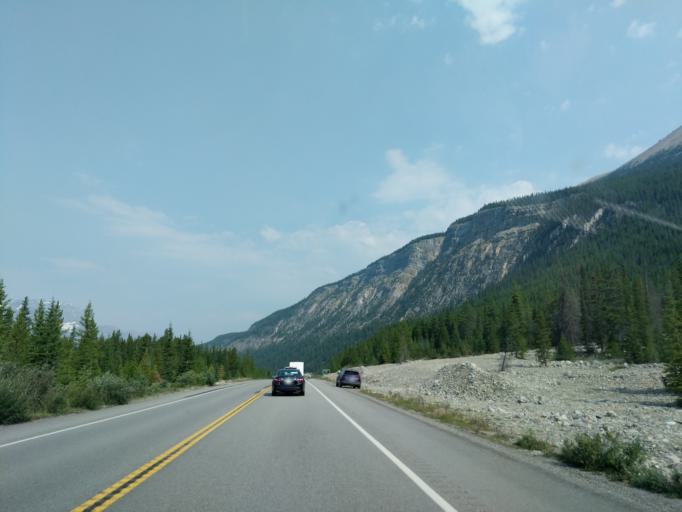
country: CA
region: Alberta
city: Lake Louise
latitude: 51.8399
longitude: -116.6155
